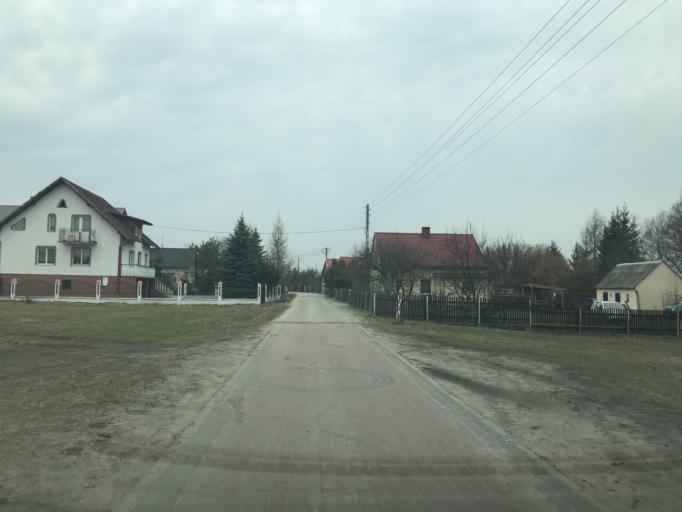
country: PL
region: Warmian-Masurian Voivodeship
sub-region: Powiat dzialdowski
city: Lidzbark
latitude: 53.3016
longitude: 19.8591
